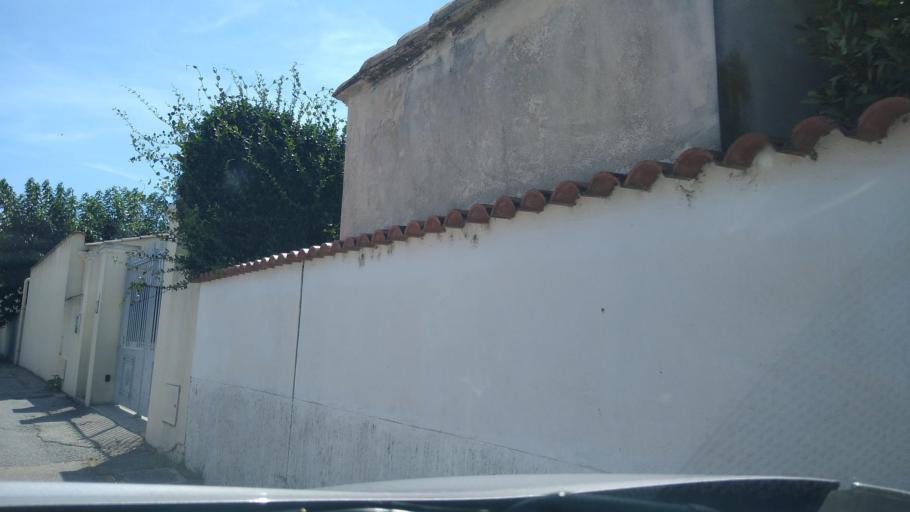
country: FR
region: Languedoc-Roussillon
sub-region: Departement du Gard
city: Aigues-Mortes
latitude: 43.5684
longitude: 4.1852
